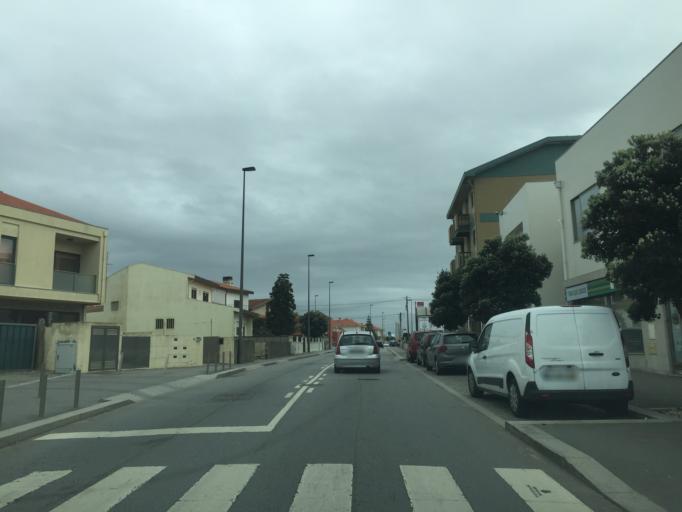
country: PT
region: Porto
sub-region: Matosinhos
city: Lavra
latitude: 41.2381
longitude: -8.7228
